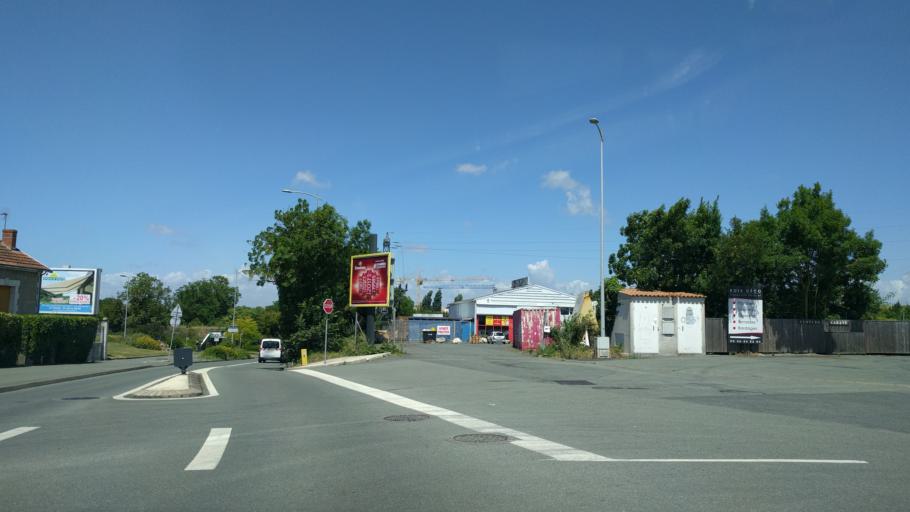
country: FR
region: Poitou-Charentes
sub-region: Departement de la Charente-Maritime
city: Perigny
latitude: 46.1601
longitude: -1.1226
